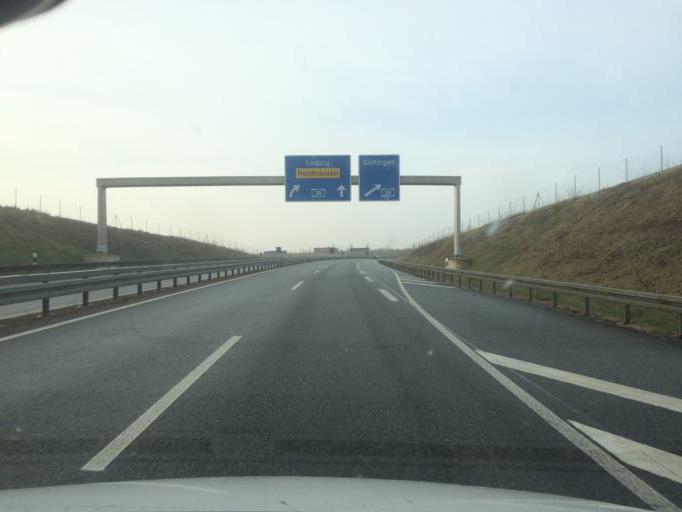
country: DE
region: Thuringia
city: Nohra
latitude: 51.4934
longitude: 10.7180
